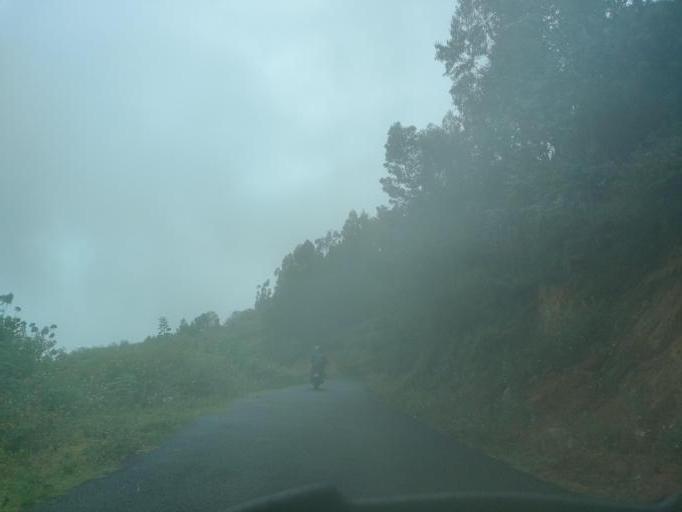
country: IN
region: Tamil Nadu
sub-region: Dindigul
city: Kodaikanal
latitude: 10.2324
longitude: 77.3322
